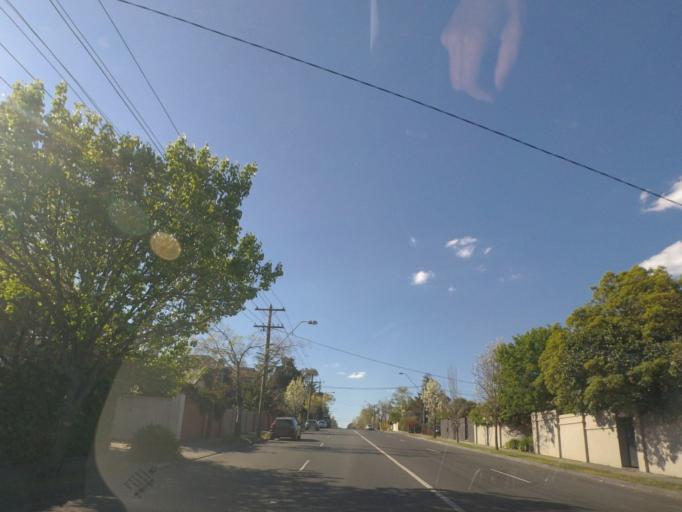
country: AU
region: Victoria
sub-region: Boroondara
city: Kew
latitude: -37.8167
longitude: 145.0272
